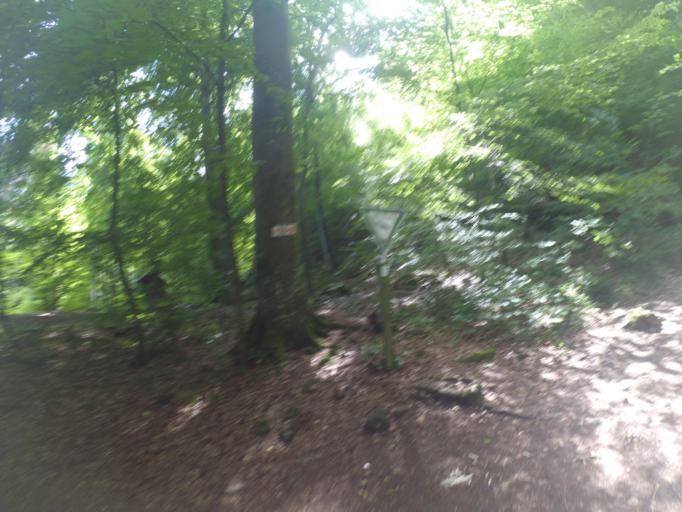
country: DE
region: Baden-Wuerttemberg
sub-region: Tuebingen Region
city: Bad Urach
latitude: 48.4827
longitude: 9.3671
